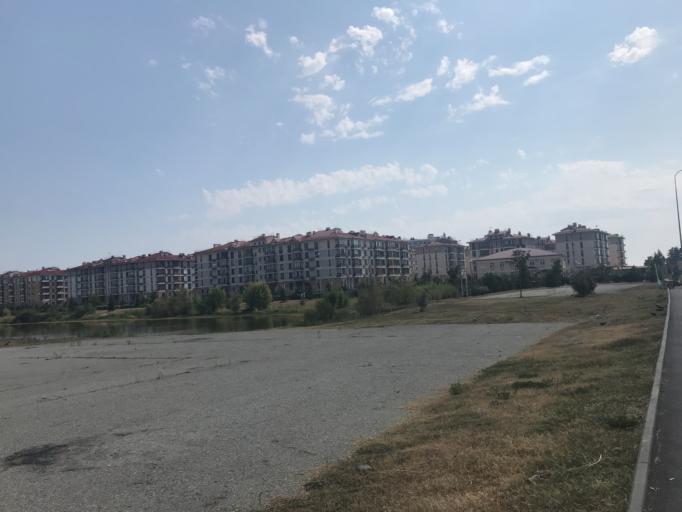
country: RU
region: Krasnodarskiy
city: Adler
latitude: 43.3995
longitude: 39.9764
